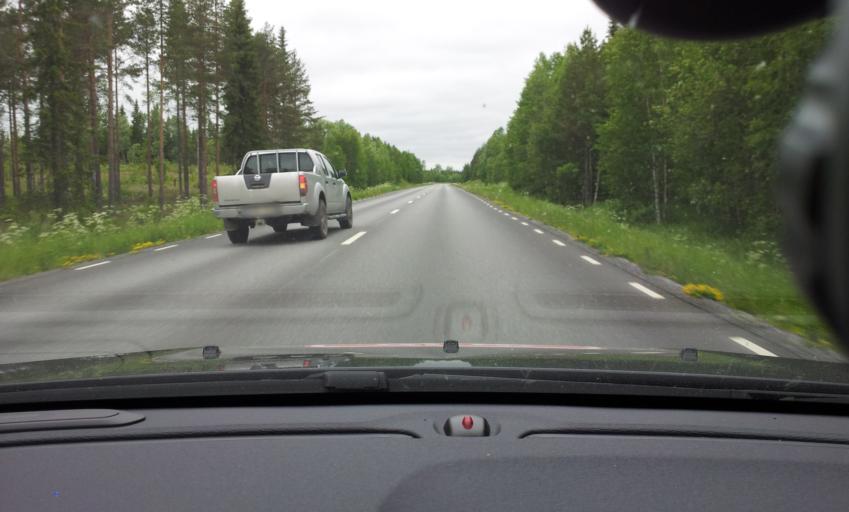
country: SE
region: Jaemtland
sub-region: Krokoms Kommun
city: Krokom
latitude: 63.0722
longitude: 14.3074
